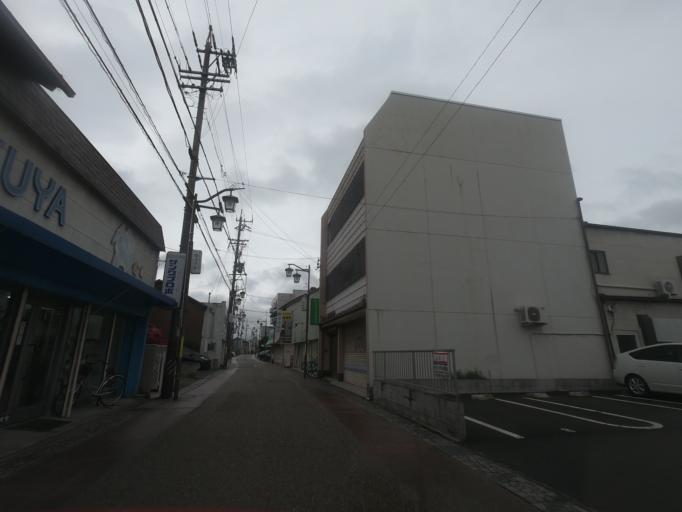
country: JP
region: Aichi
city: Kasugai
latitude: 35.2472
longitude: 136.9776
